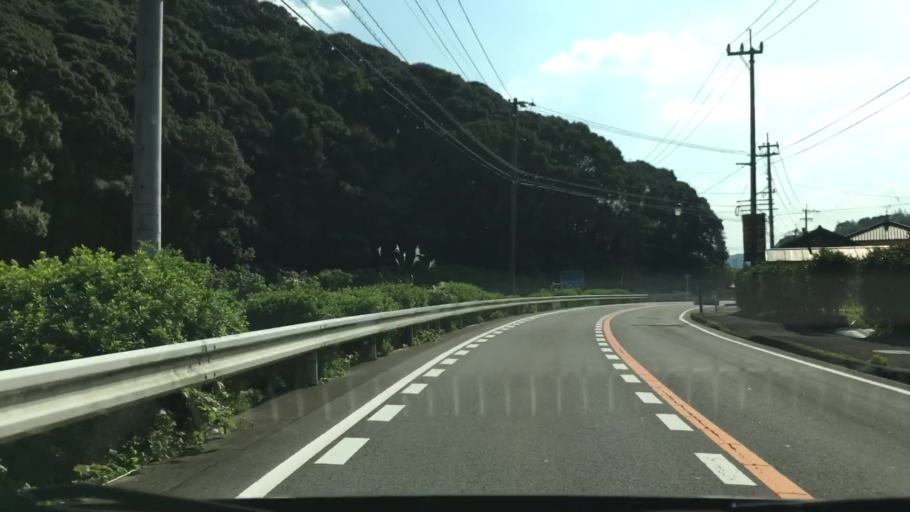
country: JP
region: Nagasaki
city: Togitsu
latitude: 32.9538
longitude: 129.7856
